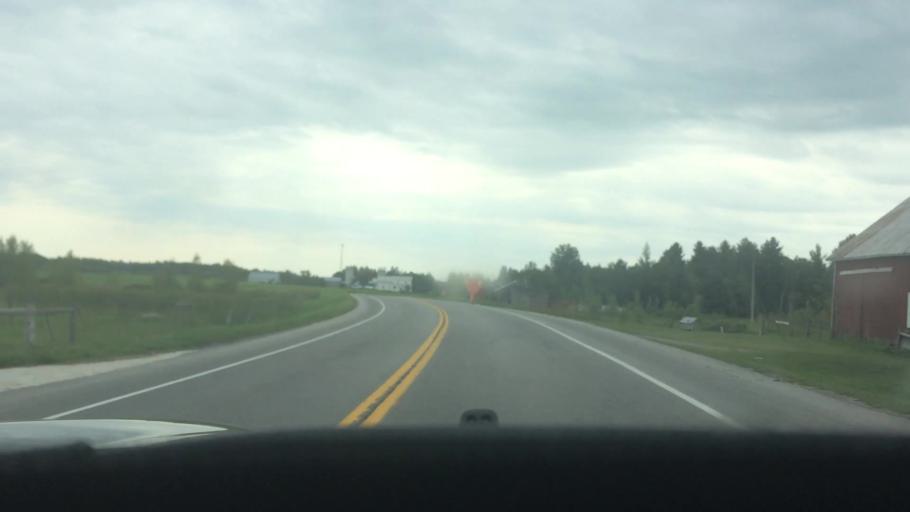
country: US
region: New York
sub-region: St. Lawrence County
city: Ogdensburg
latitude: 44.5752
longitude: -75.3646
